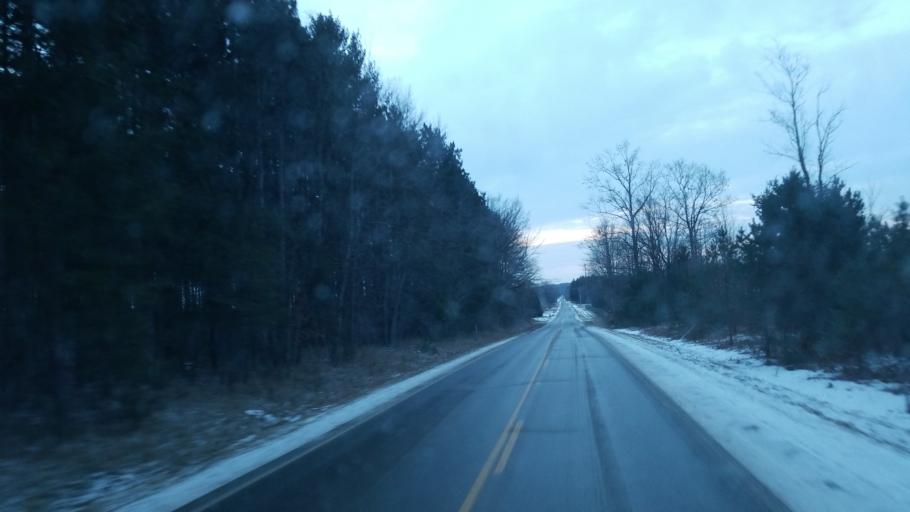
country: US
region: Michigan
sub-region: Osceola County
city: Reed City
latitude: 43.8419
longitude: -85.4242
